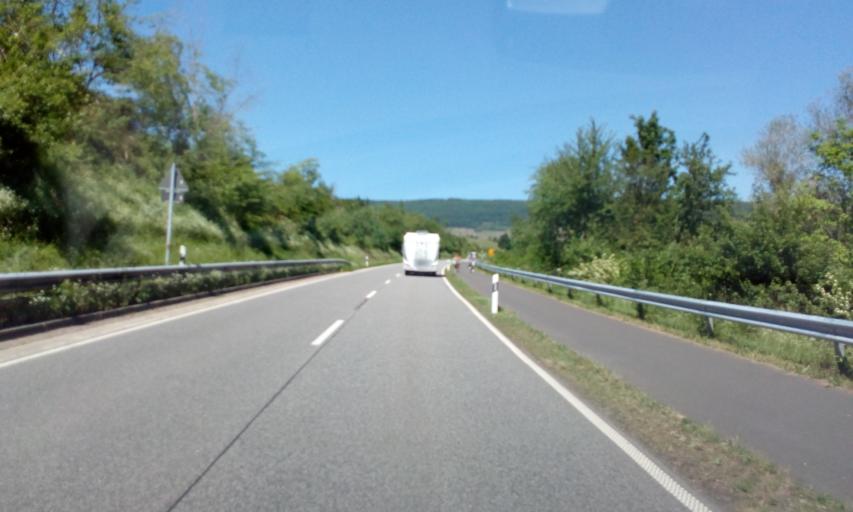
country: DE
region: Rheinland-Pfalz
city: Minheim
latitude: 49.8653
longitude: 6.9260
